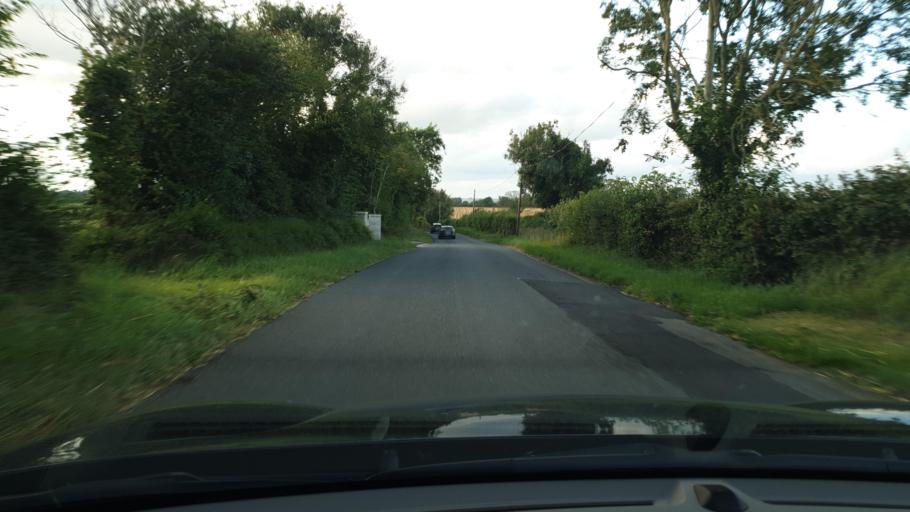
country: IE
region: Leinster
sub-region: Lu
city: Drogheda
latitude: 53.6830
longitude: -6.3320
